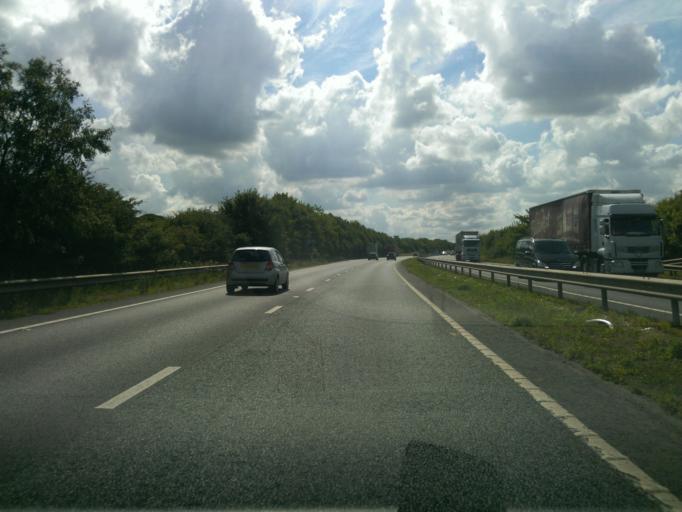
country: GB
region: England
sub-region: Northamptonshire
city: Desborough
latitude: 52.4066
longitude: -0.8448
